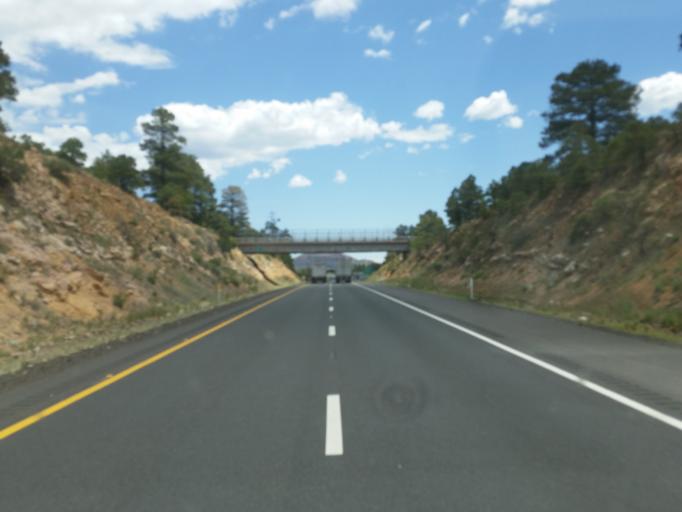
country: US
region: Arizona
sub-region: Coconino County
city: Flagstaff
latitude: 35.2007
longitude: -111.6093
